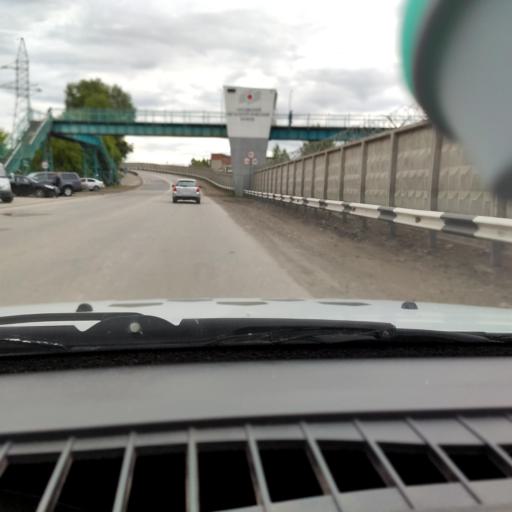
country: RU
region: Perm
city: Chusovoy
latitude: 58.2901
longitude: 57.8150
